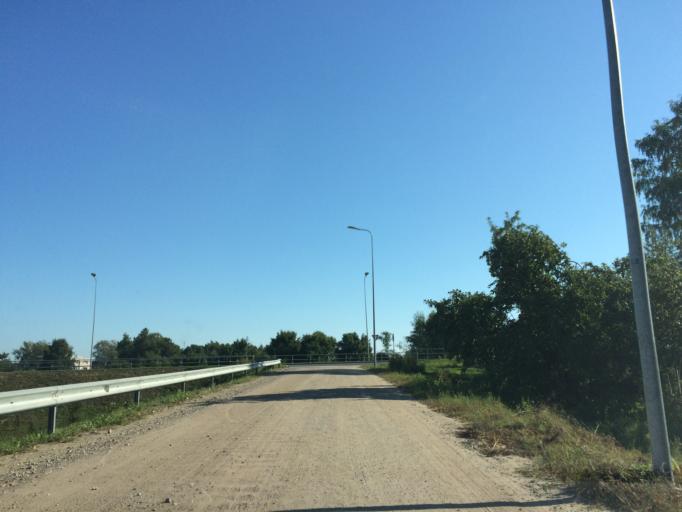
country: LV
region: Rezekne
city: Rezekne
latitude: 56.5128
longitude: 27.3565
